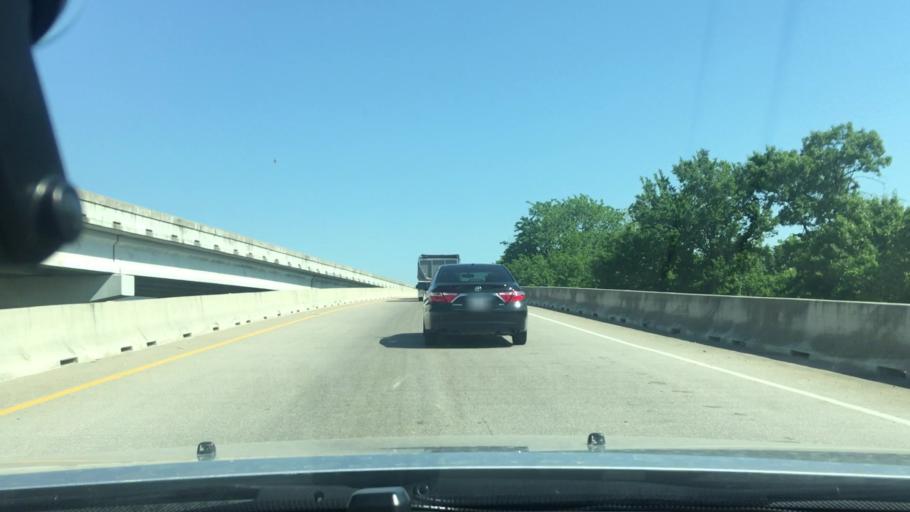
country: US
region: Texas
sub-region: Denton County
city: Denton
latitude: 33.2342
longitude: -97.0895
